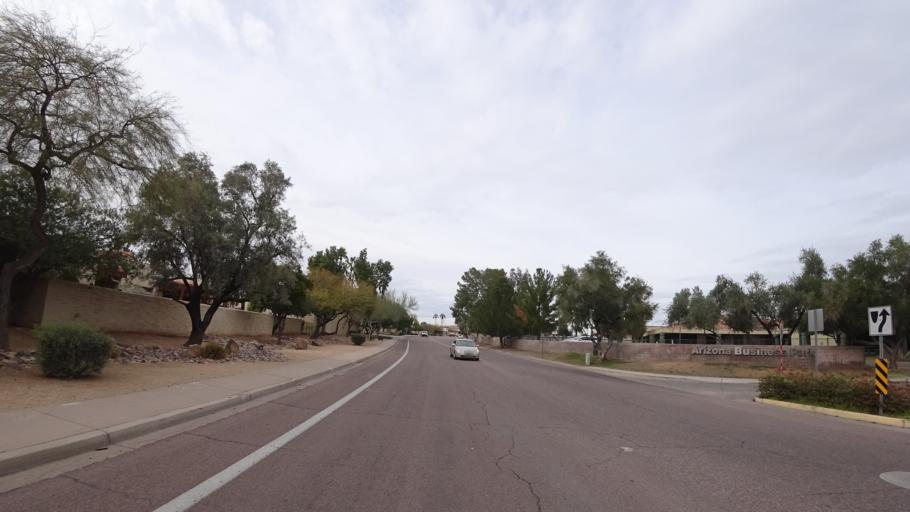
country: US
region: Arizona
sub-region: Maricopa County
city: Glendale
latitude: 33.6366
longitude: -112.1206
